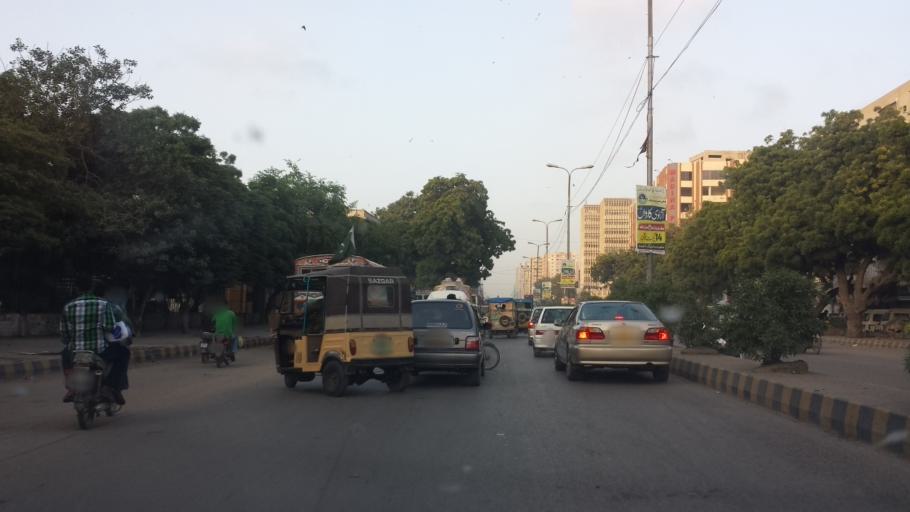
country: PK
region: Sindh
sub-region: Karachi District
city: Karachi
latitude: 24.8616
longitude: 67.0190
